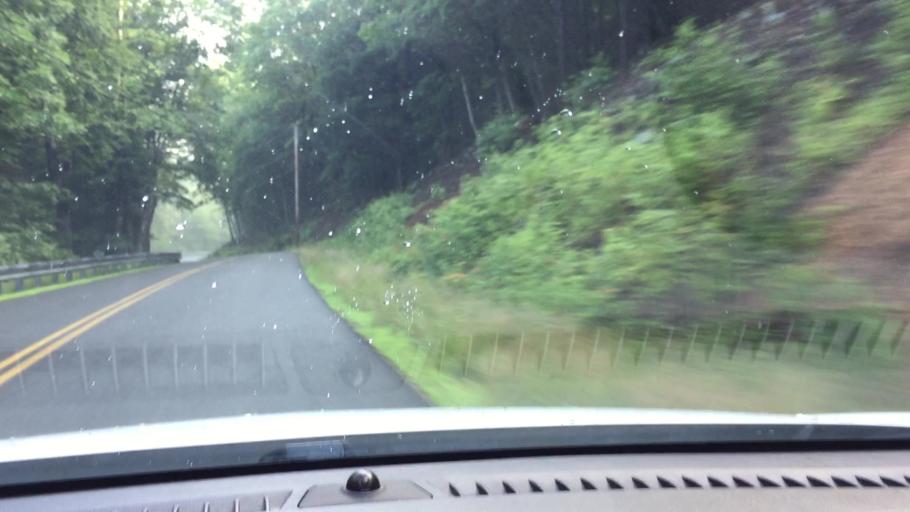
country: US
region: Massachusetts
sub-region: Berkshire County
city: Becket
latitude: 42.3989
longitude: -72.9802
